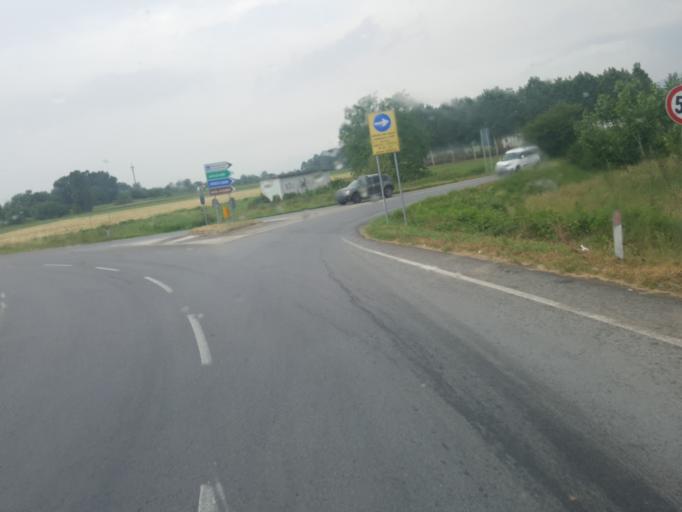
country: IT
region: Piedmont
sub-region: Provincia di Torino
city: Candiolo
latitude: 44.9627
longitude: 7.5770
